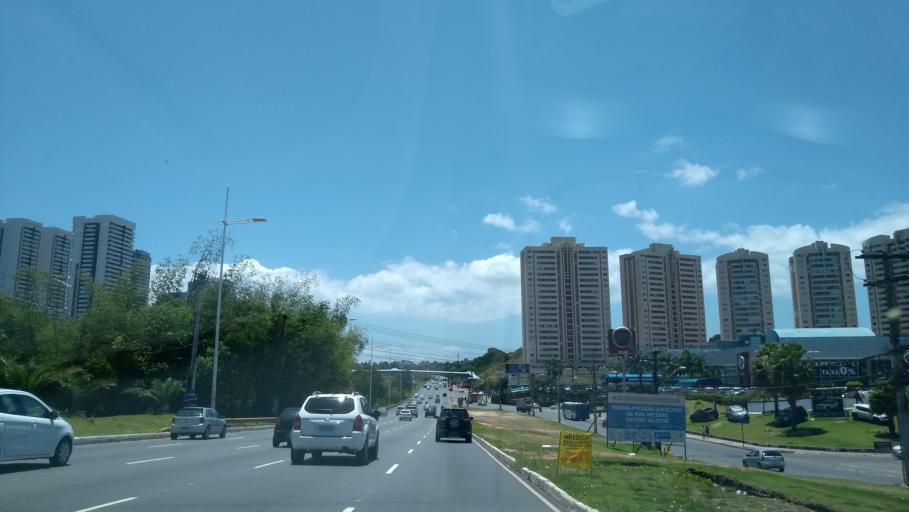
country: BR
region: Bahia
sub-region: Lauro De Freitas
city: Lauro de Freitas
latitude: -12.9380
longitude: -38.4089
